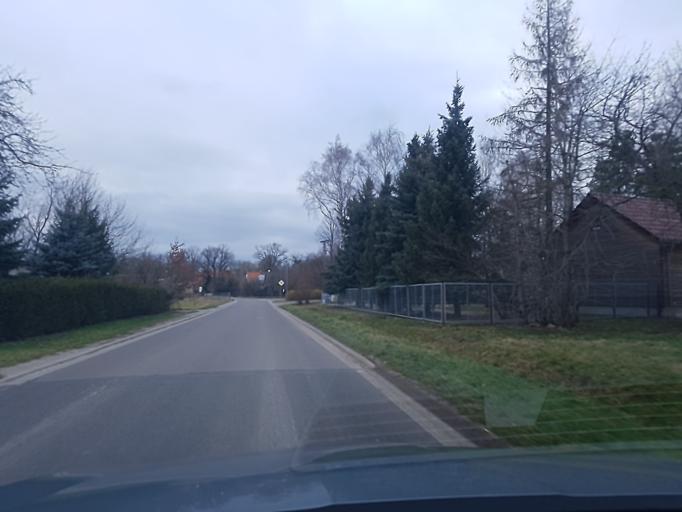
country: DE
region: Brandenburg
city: Sonnewalde
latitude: 51.6878
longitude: 13.6826
